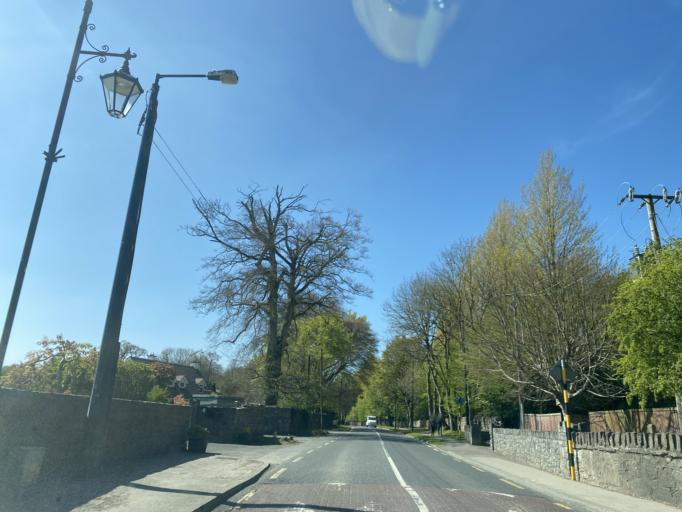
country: IE
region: Leinster
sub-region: Kildare
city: Kill
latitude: 53.3103
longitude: -6.6095
